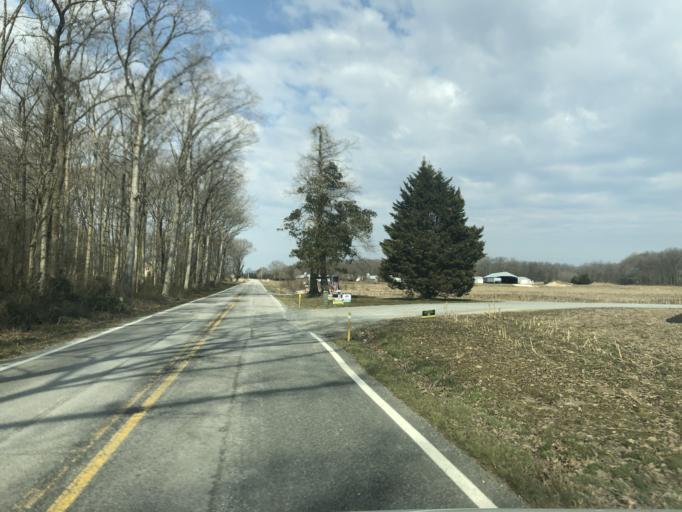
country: US
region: Maryland
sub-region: Queen Anne's County
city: Centreville
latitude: 39.0851
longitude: -75.9369
